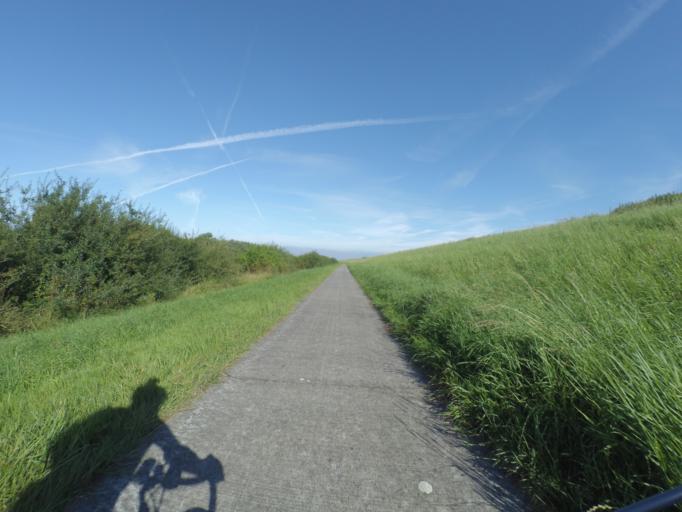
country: NL
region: Flevoland
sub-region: Gemeente Lelystad
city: Lelystad
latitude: 52.4189
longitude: 5.4774
